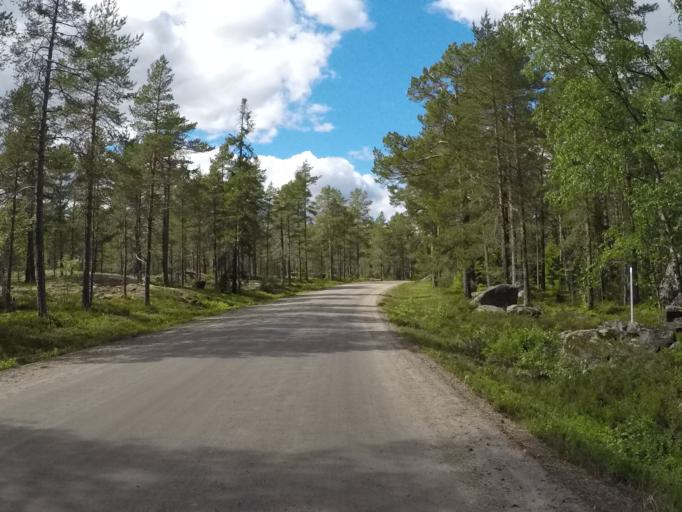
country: SE
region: Vaesterbotten
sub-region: Robertsfors Kommun
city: Robertsfors
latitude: 64.0227
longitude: 20.8943
